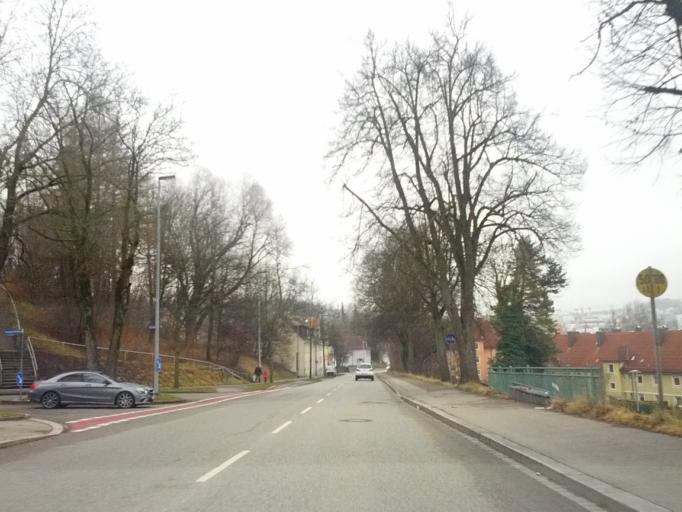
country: DE
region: Bavaria
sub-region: Swabia
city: Kempten (Allgaeu)
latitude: 47.7305
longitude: 10.3231
